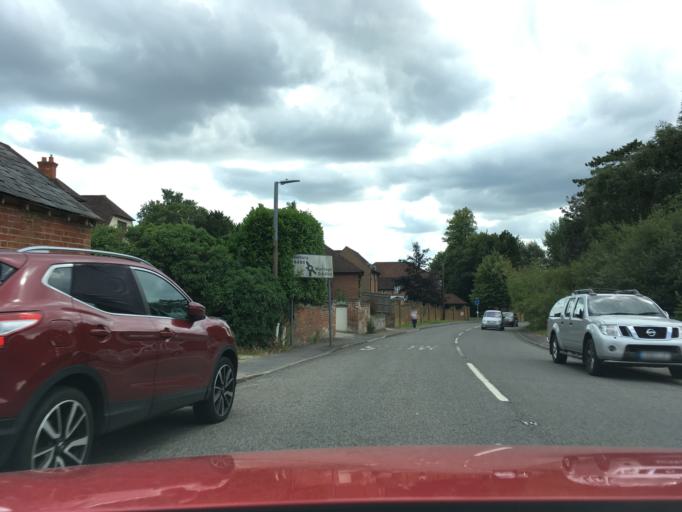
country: GB
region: England
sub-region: West Berkshire
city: Newbury
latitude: 51.4187
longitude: -1.3284
